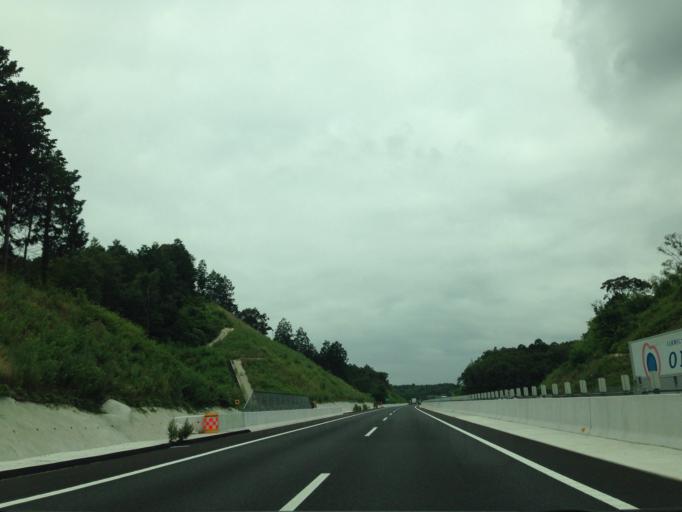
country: JP
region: Aichi
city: Okazaki
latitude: 34.9788
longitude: 137.2424
